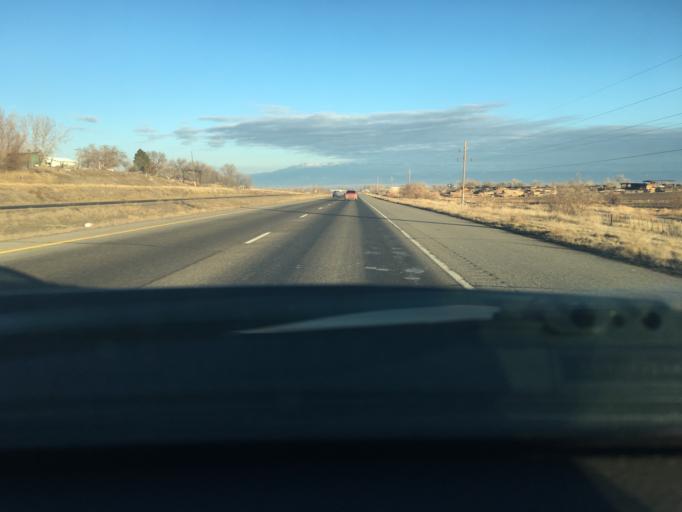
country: US
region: Colorado
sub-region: Montrose County
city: Olathe
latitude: 38.5822
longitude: -107.9654
